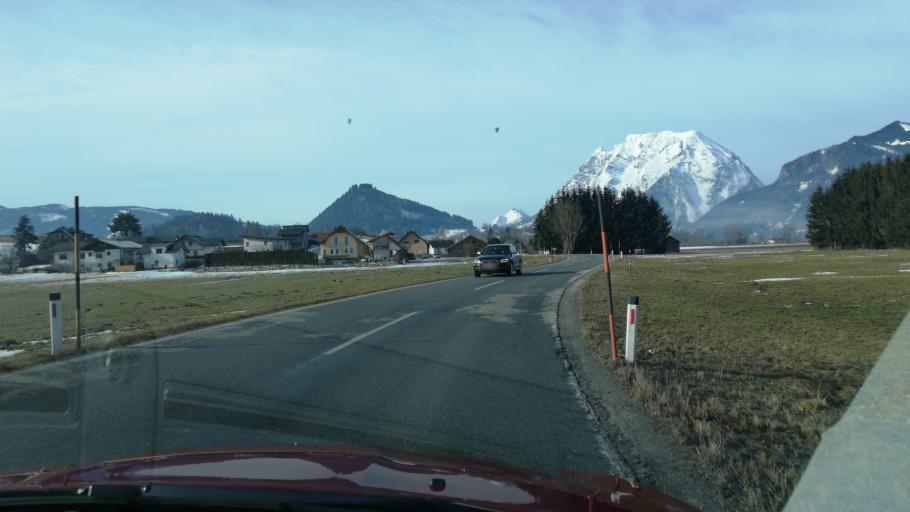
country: AT
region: Styria
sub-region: Politischer Bezirk Liezen
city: Worschach
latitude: 47.5327
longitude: 14.1551
